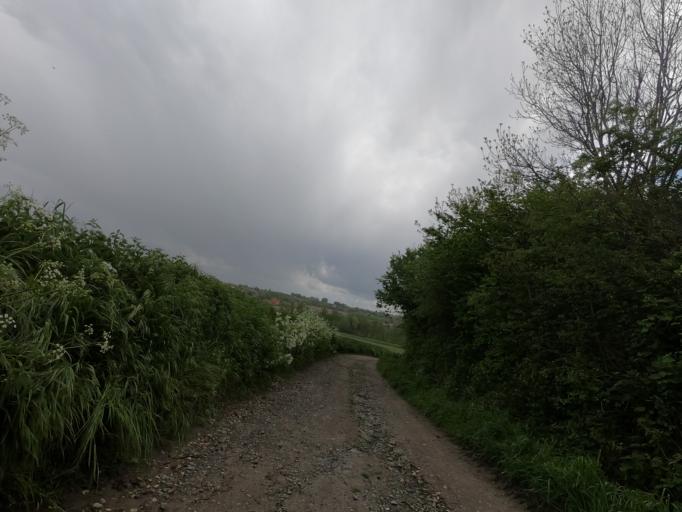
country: BE
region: Flanders
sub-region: Provincie Oost-Vlaanderen
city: Ronse
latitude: 50.7785
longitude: 3.5576
